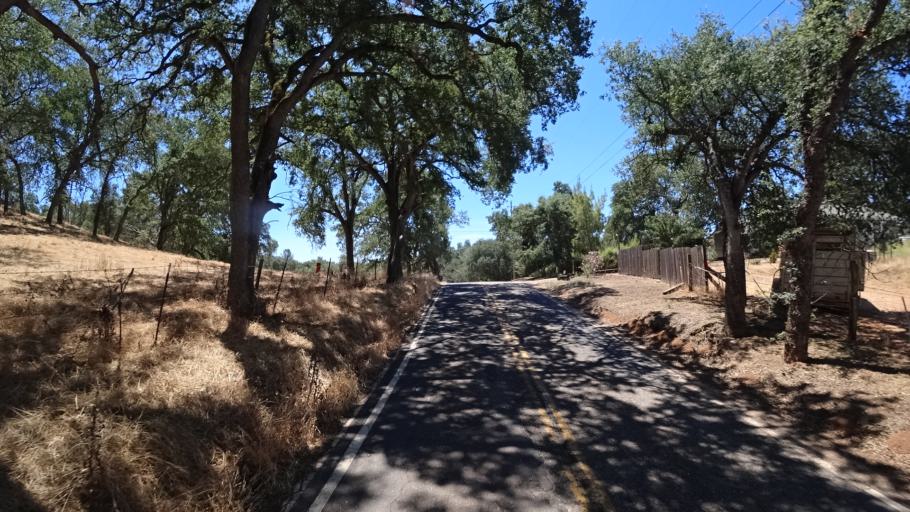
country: US
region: California
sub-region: Calaveras County
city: Valley Springs
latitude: 38.2149
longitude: -120.8622
